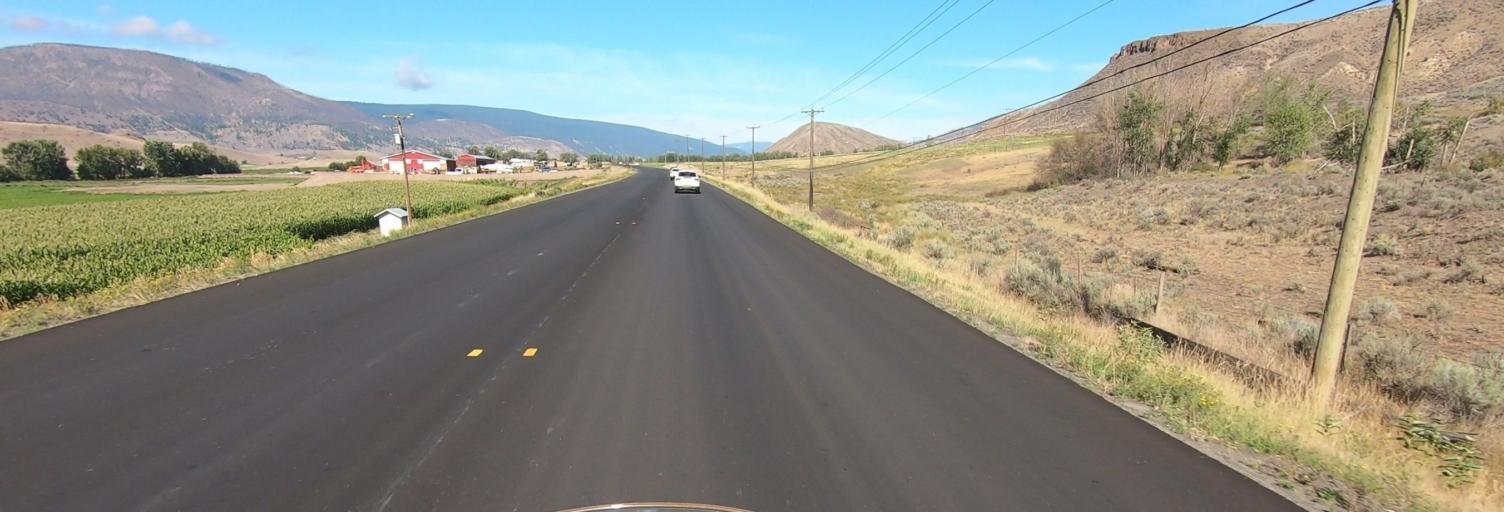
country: CA
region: British Columbia
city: Cache Creek
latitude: 50.8017
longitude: -121.2692
